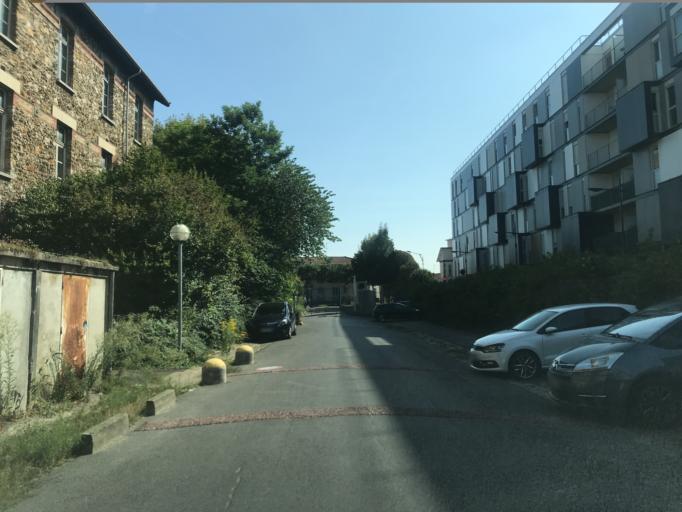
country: FR
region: Ile-de-France
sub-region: Departement du Val-de-Marne
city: Villejuif
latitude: 48.7954
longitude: 2.3603
